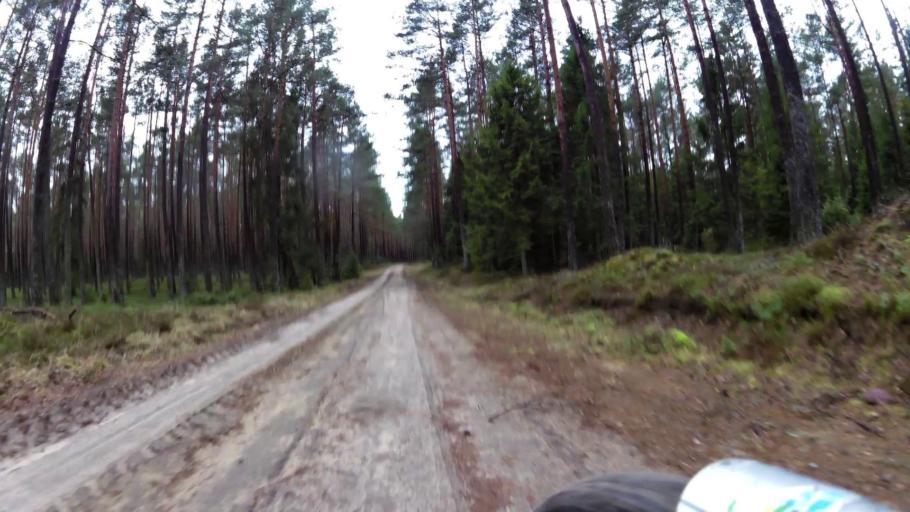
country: PL
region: Pomeranian Voivodeship
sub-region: Powiat bytowski
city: Borzytuchom
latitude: 54.2578
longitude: 17.3776
